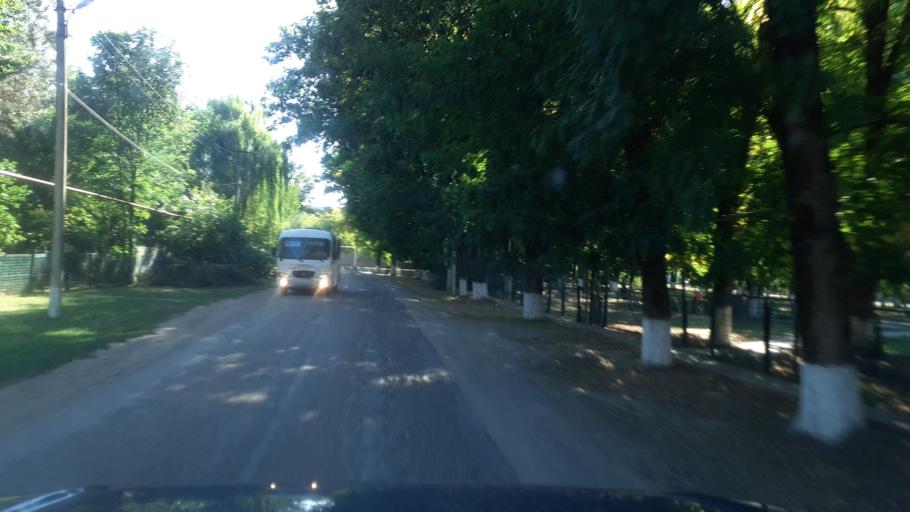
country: RU
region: Krasnodarskiy
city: Azovskaya
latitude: 44.7379
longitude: 38.5408
